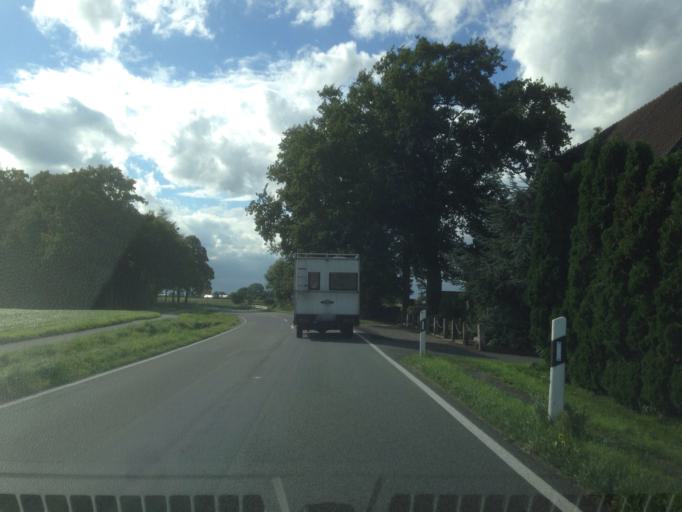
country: DE
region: North Rhine-Westphalia
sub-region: Regierungsbezirk Munster
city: Senden
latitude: 51.8247
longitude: 7.5285
